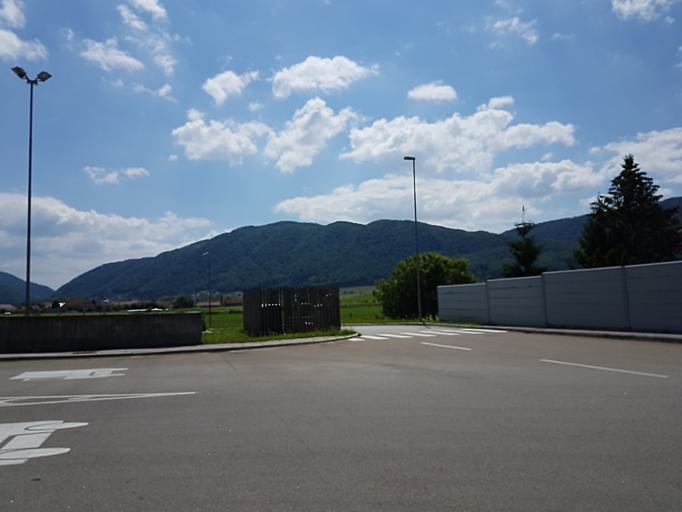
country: SI
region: Bistrica ob Sotli
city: Bistrica ob Sotli
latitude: 46.0695
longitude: 15.6608
